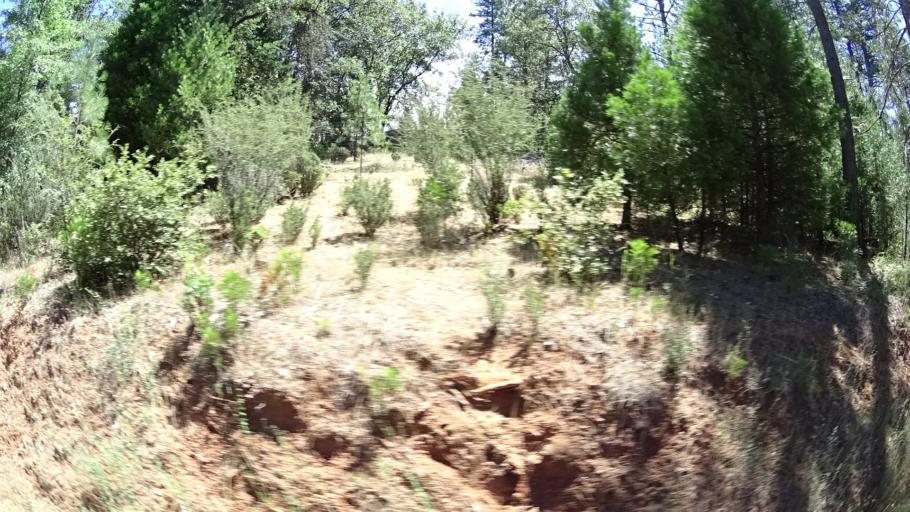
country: US
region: California
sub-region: Amador County
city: Pioneer
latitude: 38.3511
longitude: -120.5205
